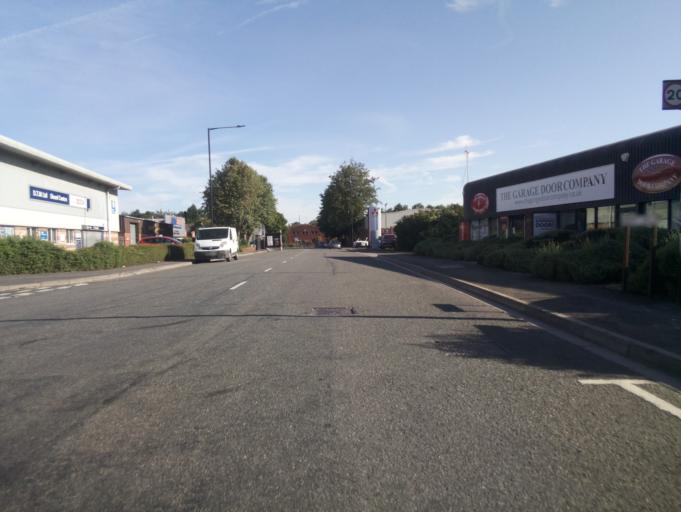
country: GB
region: England
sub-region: Bristol
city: Bristol
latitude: 51.4484
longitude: -2.5701
